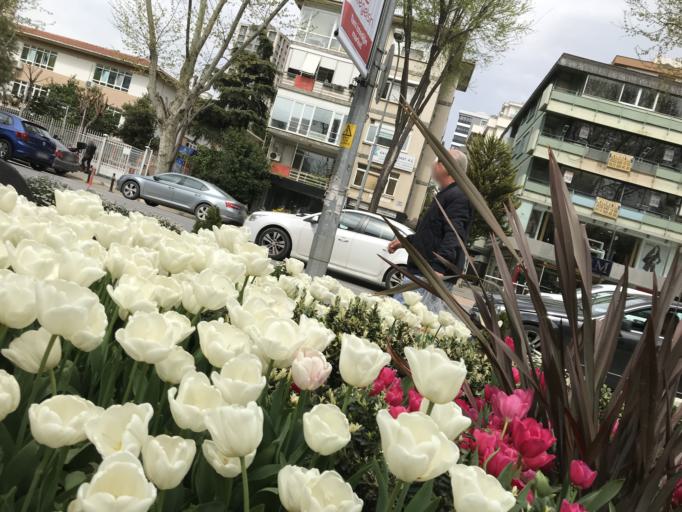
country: TR
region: Istanbul
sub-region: Atasehir
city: Atasehir
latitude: 40.9721
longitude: 29.0585
